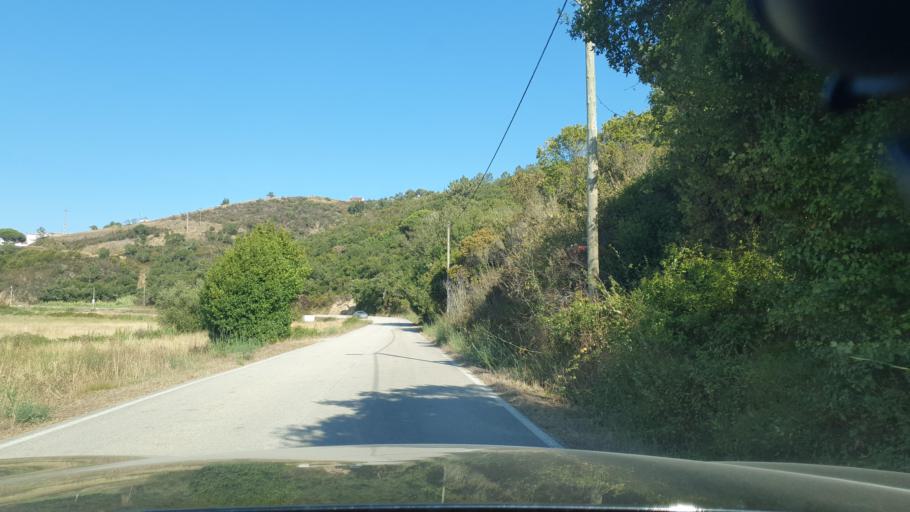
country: PT
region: Beja
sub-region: Odemira
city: Sao Teotonio
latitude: 37.4312
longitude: -8.7783
